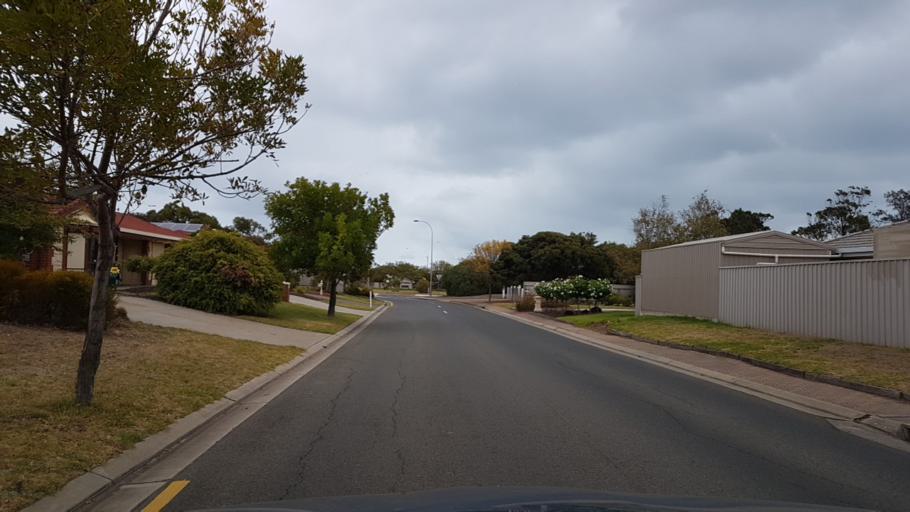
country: AU
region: South Australia
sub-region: Onkaparinga
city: Moana
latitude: -35.1944
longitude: 138.4826
